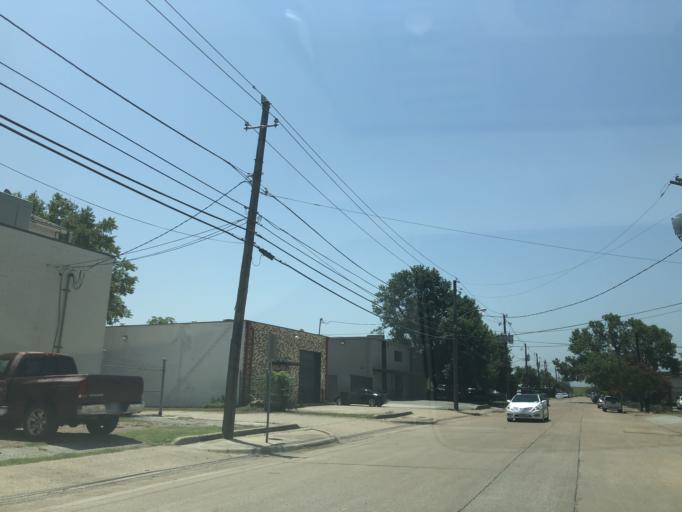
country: US
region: Texas
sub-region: Dallas County
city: Dallas
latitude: 32.8073
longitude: -96.8512
